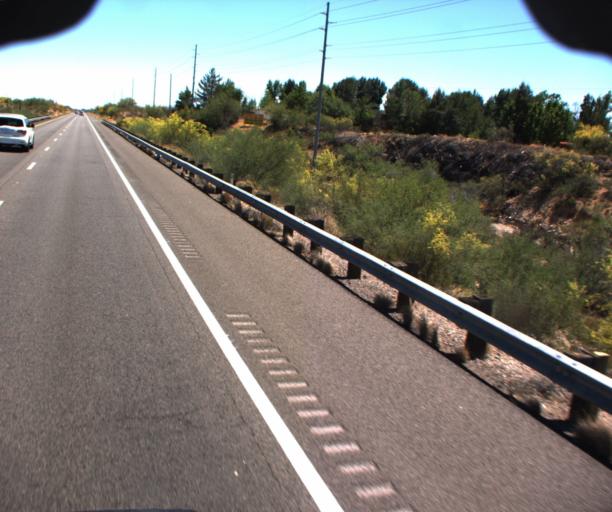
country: US
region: Arizona
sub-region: Maricopa County
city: Wickenburg
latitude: 33.8714
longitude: -112.6429
